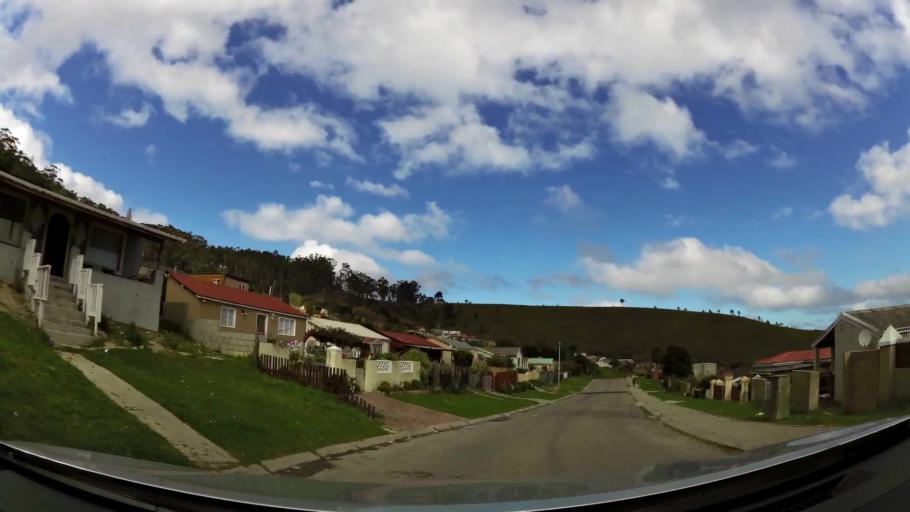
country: ZA
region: Western Cape
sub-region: Eden District Municipality
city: Knysna
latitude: -34.0522
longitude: 23.1057
